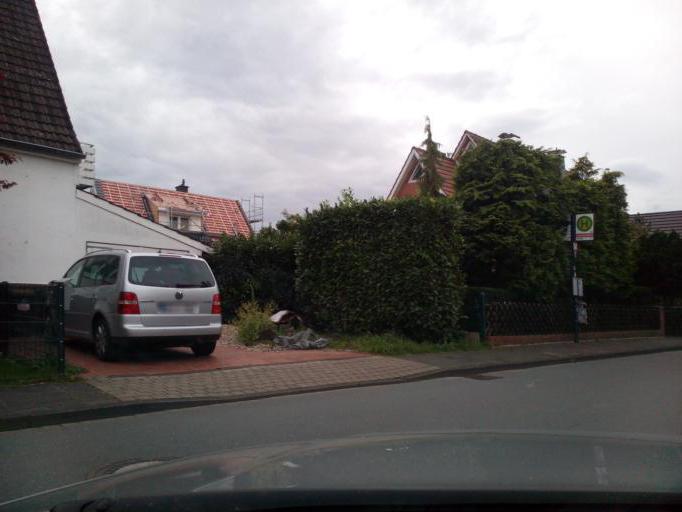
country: DE
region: North Rhine-Westphalia
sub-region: Regierungsbezirk Munster
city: Muenster
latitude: 51.9373
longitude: 7.5979
